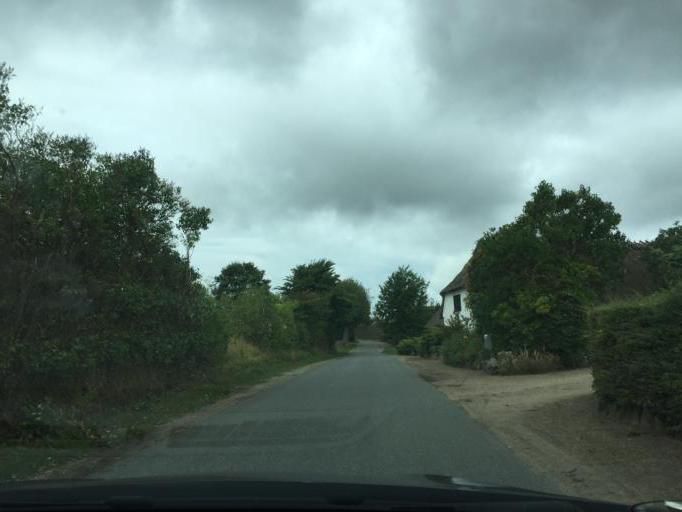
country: DK
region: South Denmark
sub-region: Assens Kommune
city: Harby
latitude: 55.1919
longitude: 10.1425
